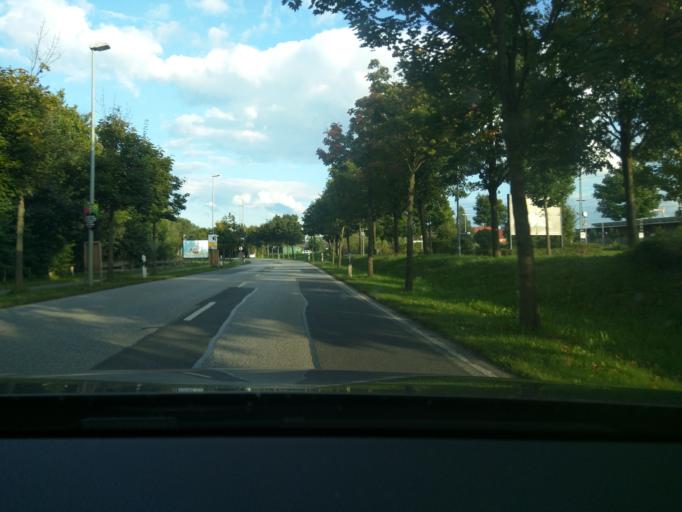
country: DE
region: Schleswig-Holstein
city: Schwarzenbek
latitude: 53.5044
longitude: 10.4847
